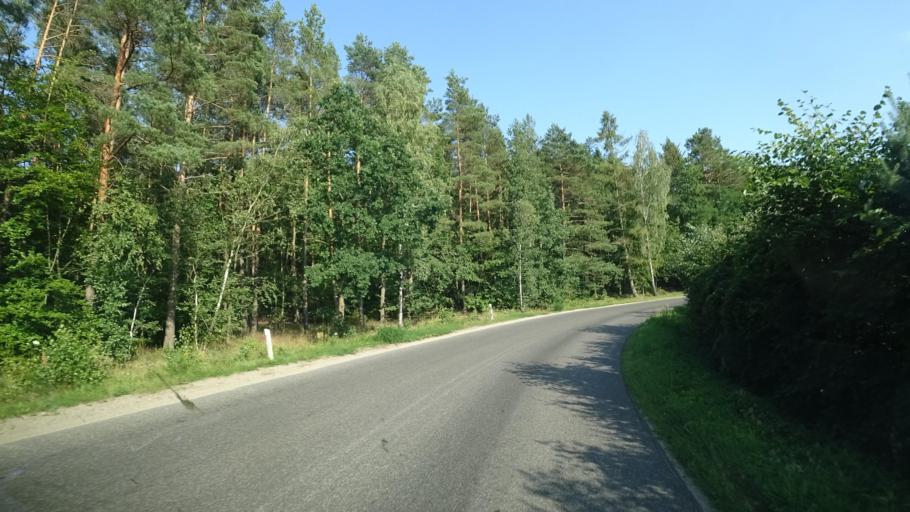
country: PL
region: Pomeranian Voivodeship
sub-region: Powiat czluchowski
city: Przechlewo
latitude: 53.7916
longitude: 17.2067
